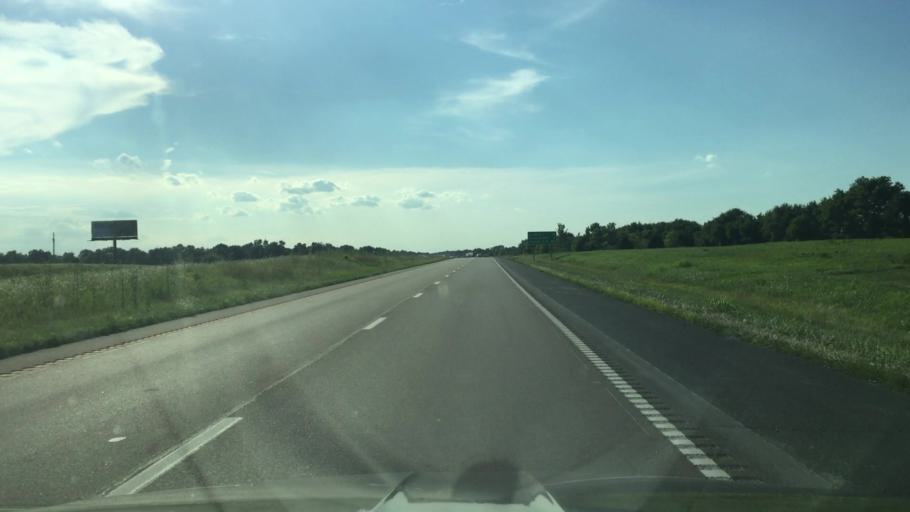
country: US
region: Missouri
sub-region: Pettis County
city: La Monte
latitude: 38.7504
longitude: -93.3472
